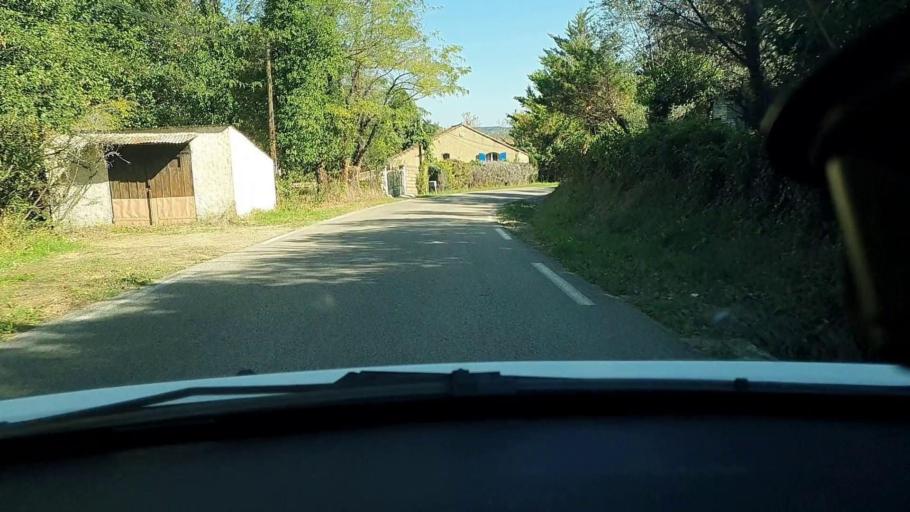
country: FR
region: Languedoc-Roussillon
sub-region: Departement du Gard
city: Saint-Julien-de-Peyrolas
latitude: 44.2855
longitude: 4.5630
